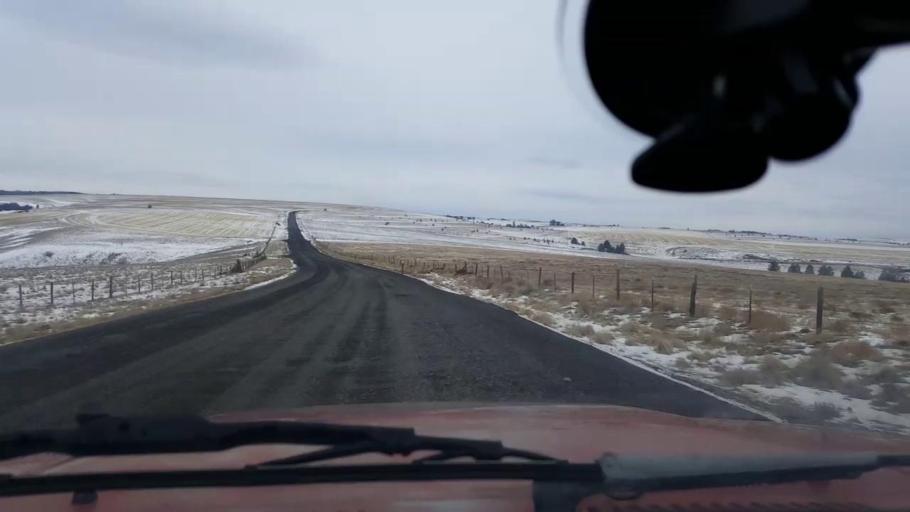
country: US
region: Washington
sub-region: Garfield County
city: Pomeroy
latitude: 46.3200
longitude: -117.4156
